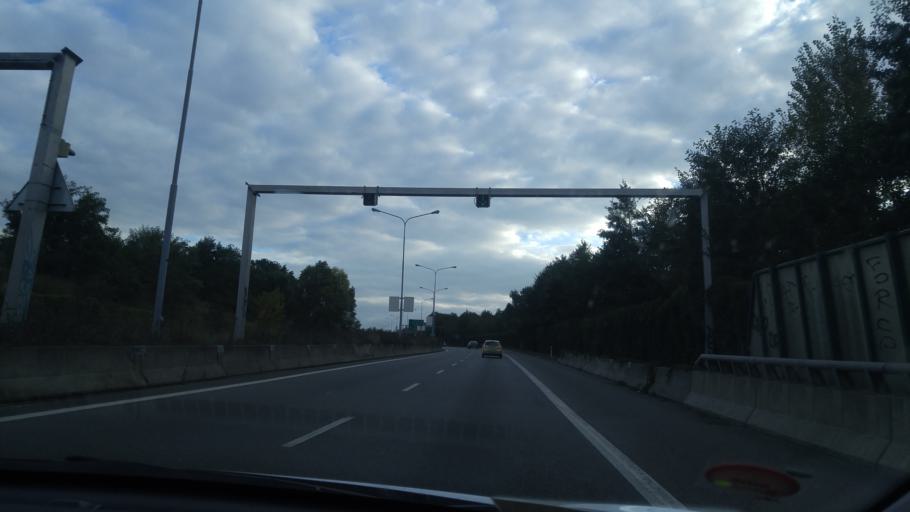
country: CZ
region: South Moravian
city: Ostopovice
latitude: 49.1830
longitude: 16.5654
